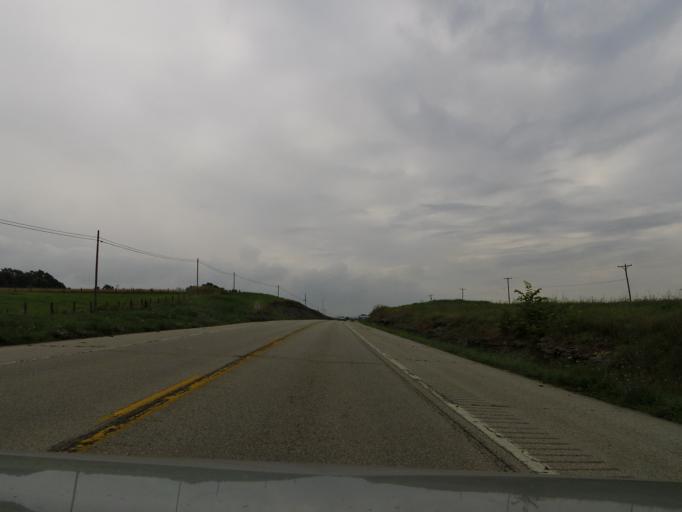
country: US
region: Kentucky
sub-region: Mason County
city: Maysville
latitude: 38.5484
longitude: -83.8234
